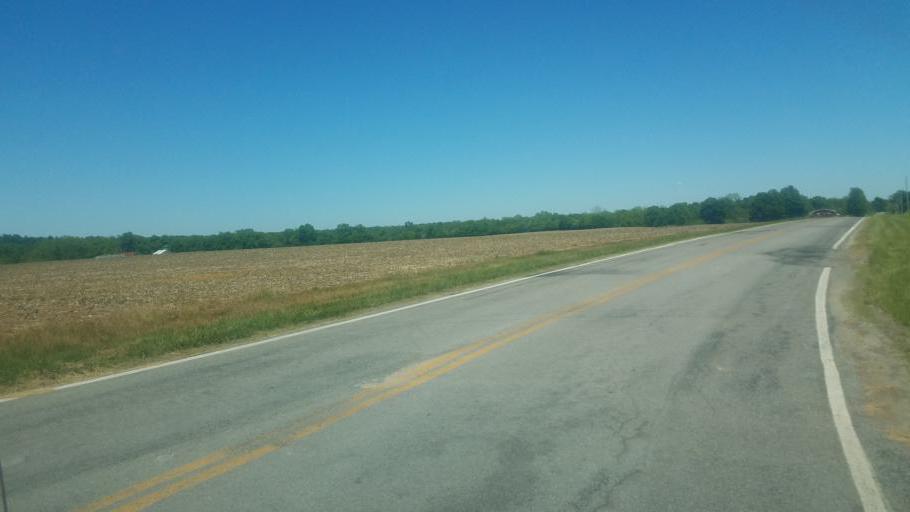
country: US
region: Ohio
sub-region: Champaign County
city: Saint Paris
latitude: 40.2074
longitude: -84.0105
